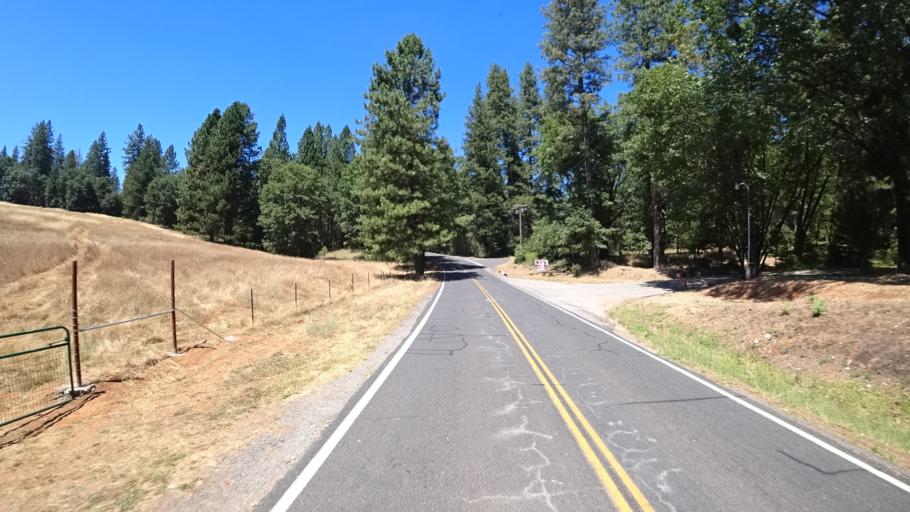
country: US
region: California
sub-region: Calaveras County
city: Mountain Ranch
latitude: 38.3298
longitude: -120.5184
